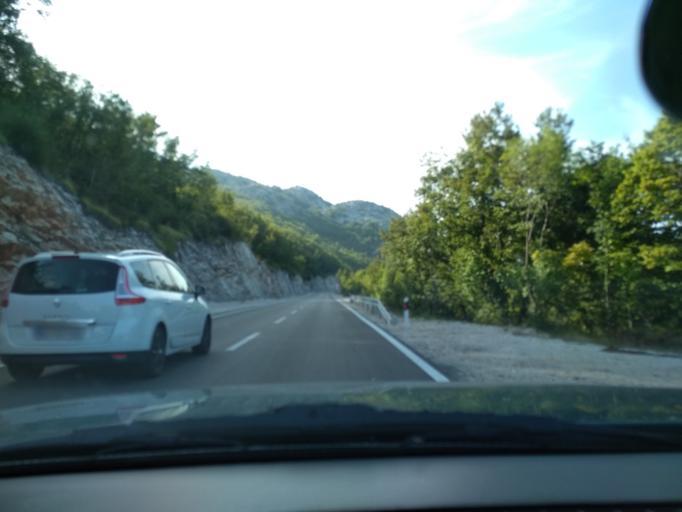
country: ME
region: Cetinje
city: Cetinje
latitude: 42.4174
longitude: 18.8782
